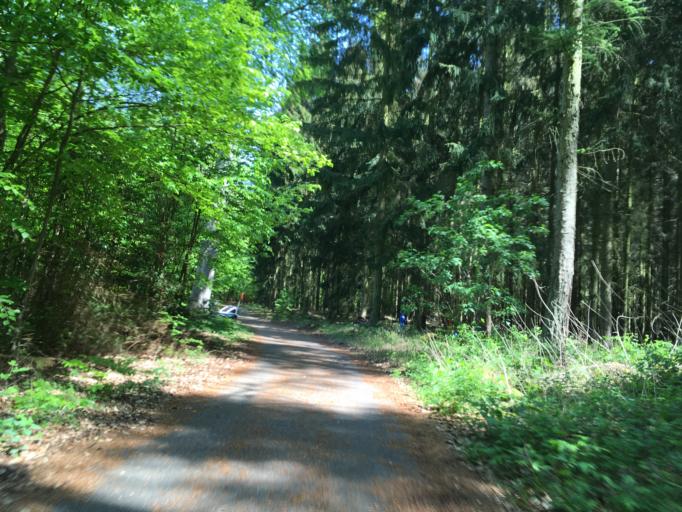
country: DE
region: Brandenburg
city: Wandlitz
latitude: 52.7416
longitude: 13.5164
